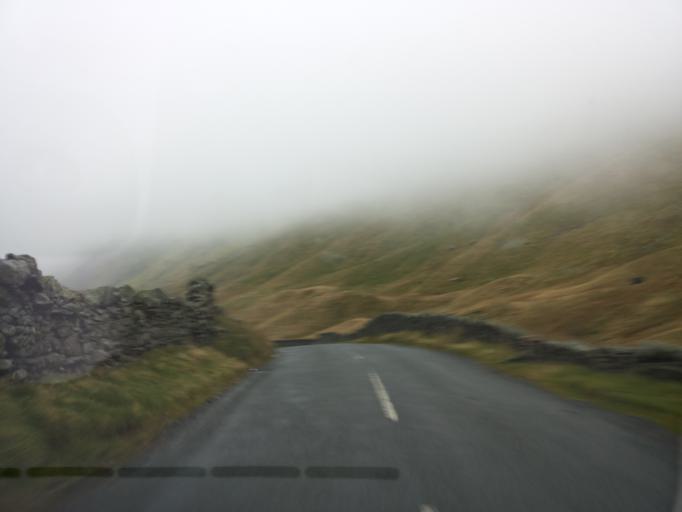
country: GB
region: England
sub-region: Cumbria
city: Ambleside
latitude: 54.4688
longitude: -2.9238
